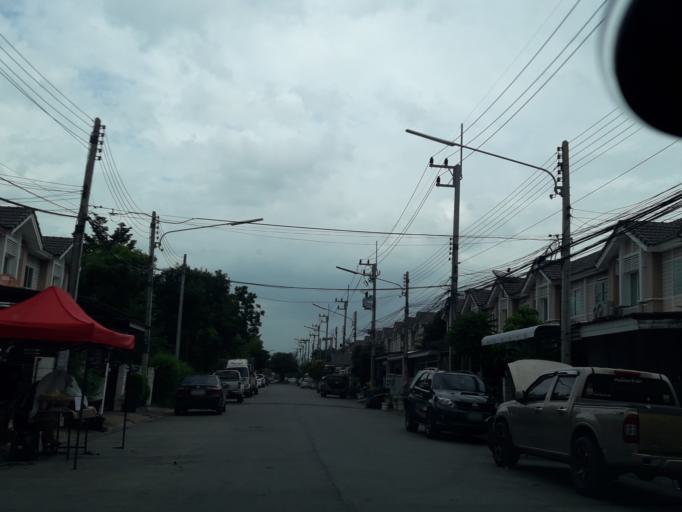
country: TH
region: Pathum Thani
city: Khlong Luang
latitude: 14.0462
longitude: 100.6686
